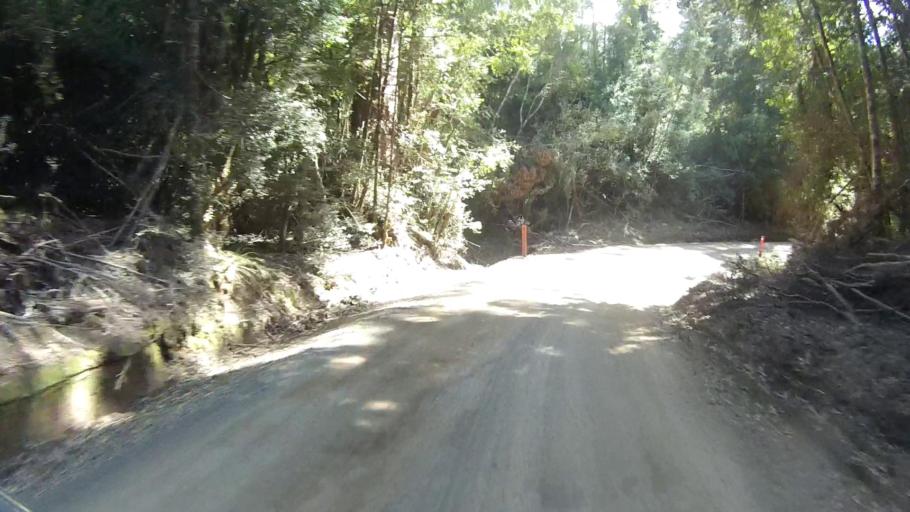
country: AU
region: Tasmania
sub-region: Derwent Valley
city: New Norfolk
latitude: -42.6818
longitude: 146.6749
